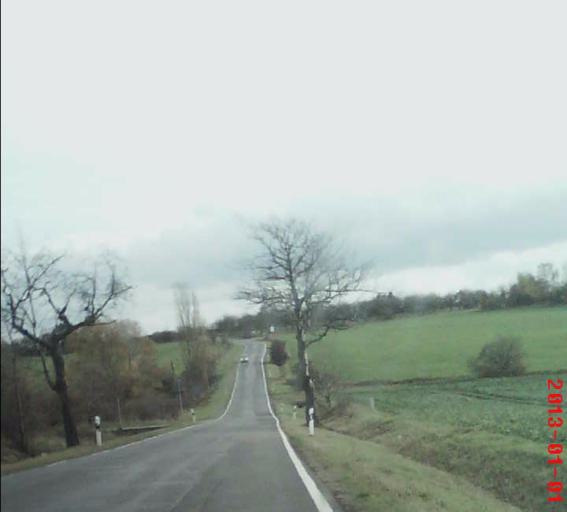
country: DE
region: Thuringia
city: Muehlhausen
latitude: 51.2300
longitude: 10.4131
